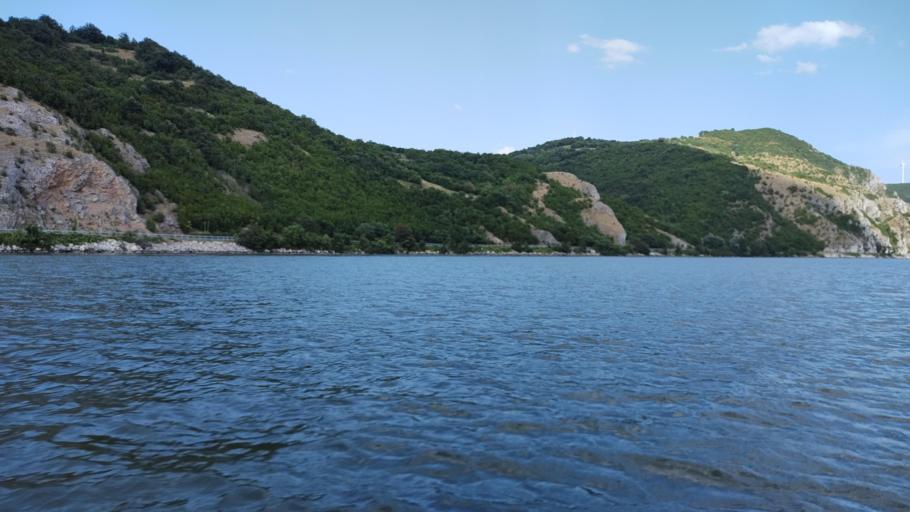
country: RO
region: Caras-Severin
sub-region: Comuna Pescari
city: Coronini
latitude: 44.6684
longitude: 21.6840
